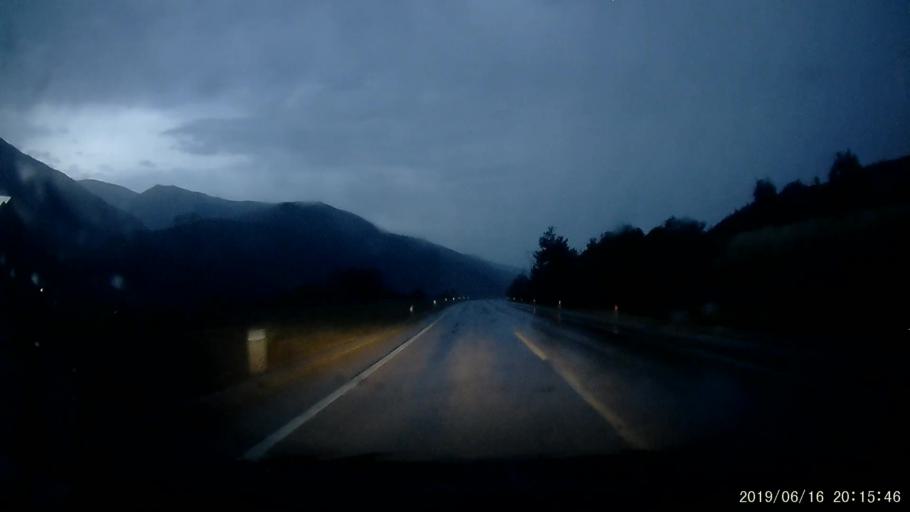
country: TR
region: Tokat
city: Resadiye
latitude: 40.3560
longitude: 37.4566
